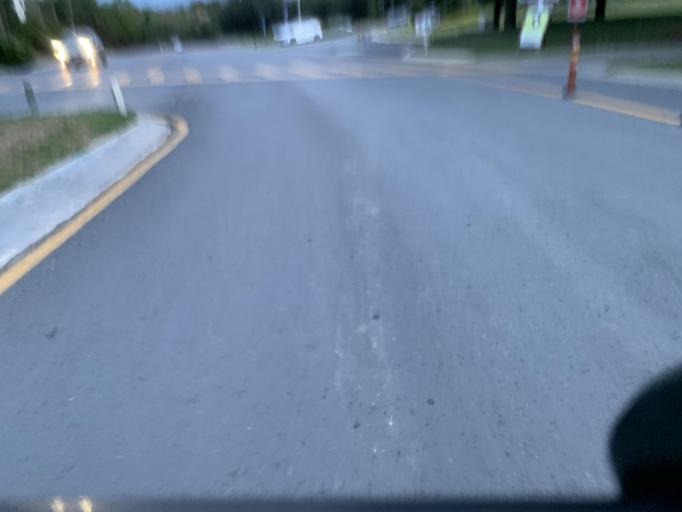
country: MX
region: Nuevo Leon
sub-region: Juarez
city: Bosques de San Pedro
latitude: 25.5170
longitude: -100.1913
